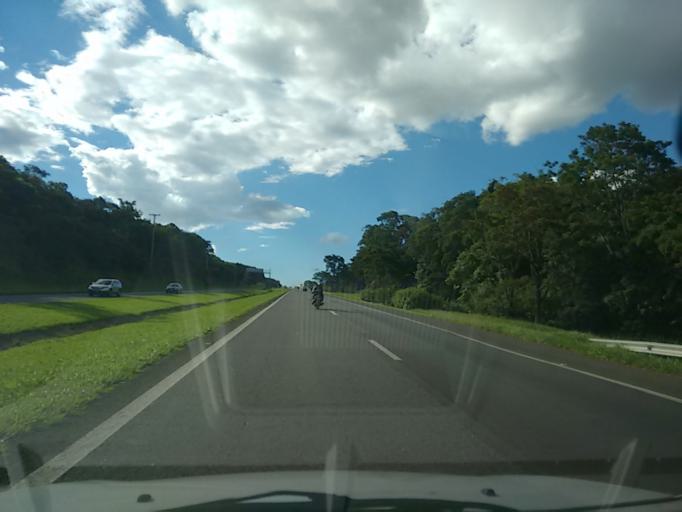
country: BR
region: Sao Paulo
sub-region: Sao Carlos
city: Sao Carlos
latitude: -22.0645
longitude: -47.8493
